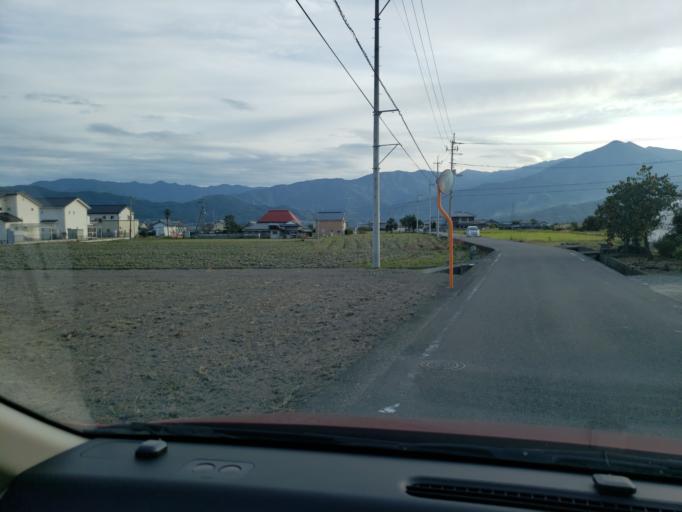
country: JP
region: Tokushima
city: Wakimachi
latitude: 34.0876
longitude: 134.2268
